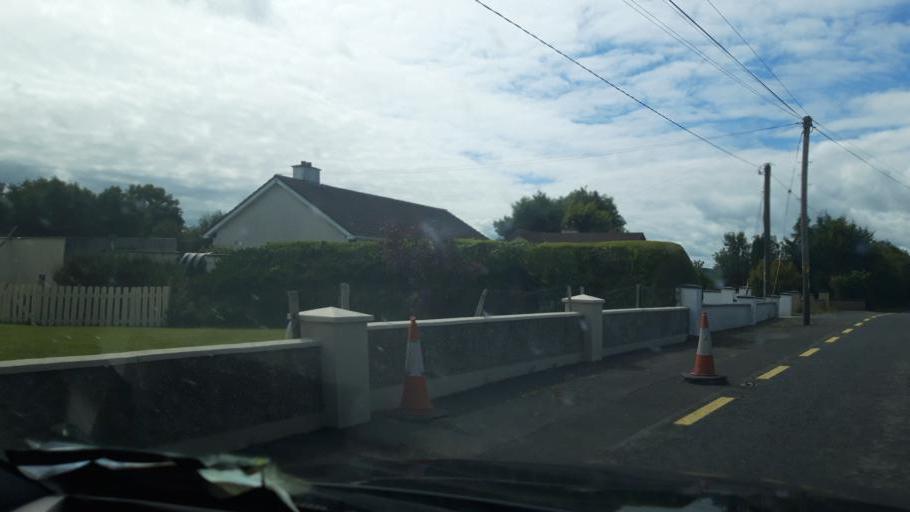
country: IE
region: Leinster
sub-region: Kilkenny
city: Callan
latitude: 52.5255
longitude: -7.4158
